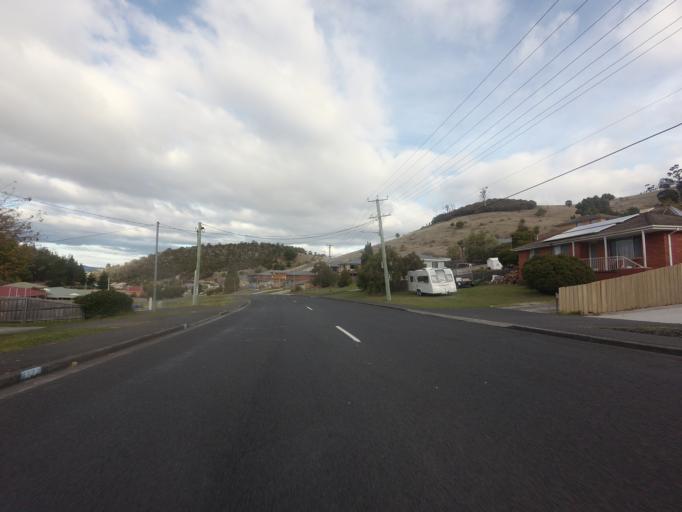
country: AU
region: Tasmania
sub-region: Glenorchy
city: Berriedale
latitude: -42.8225
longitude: 147.2476
